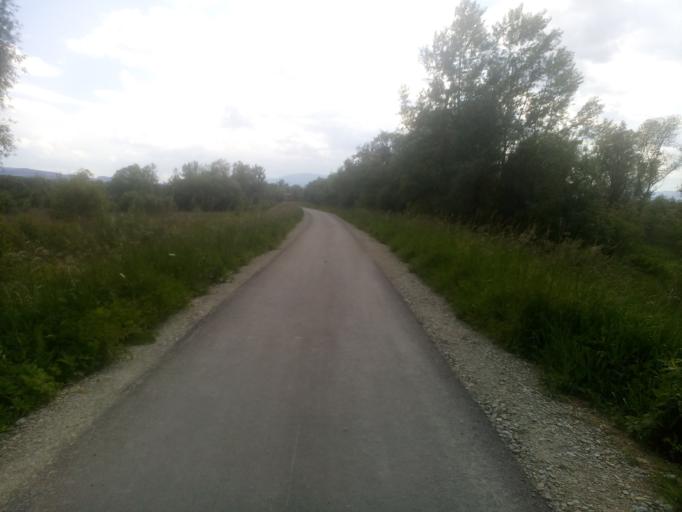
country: PL
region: Lesser Poland Voivodeship
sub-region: Powiat nowosadecki
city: Chelmiec
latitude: 49.6053
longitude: 20.6718
